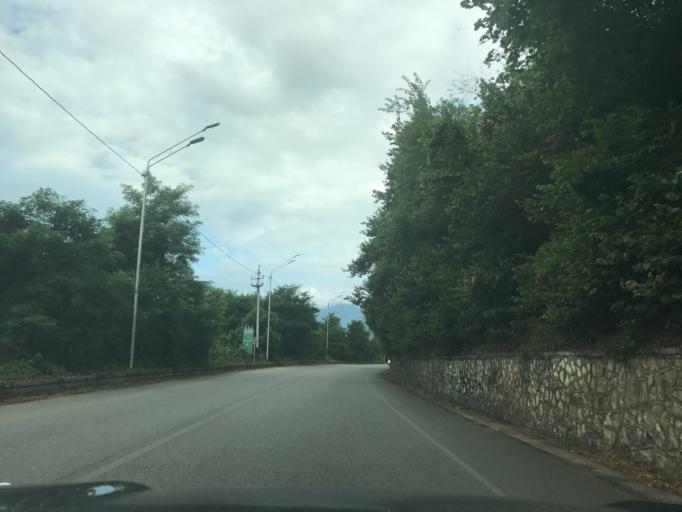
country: GE
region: Abkhazia
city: Gagra
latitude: 43.2855
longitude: 40.2727
